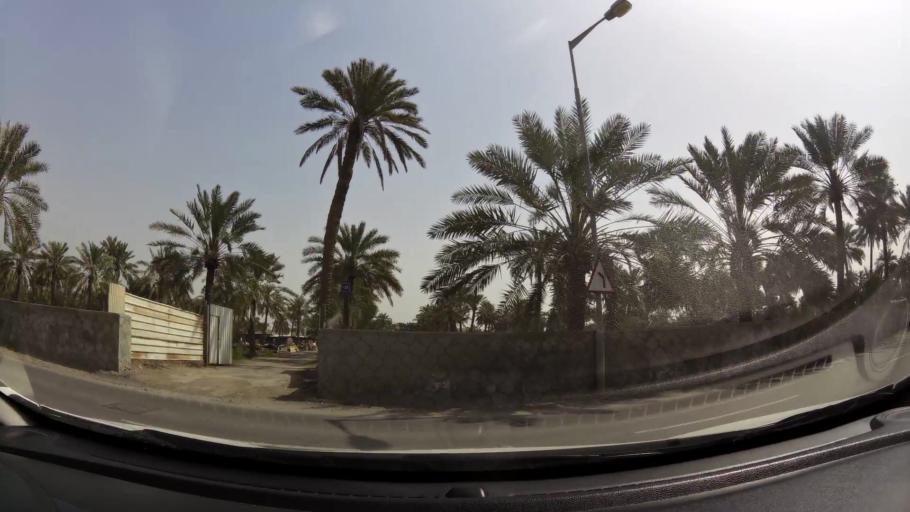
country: BH
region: Manama
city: Jidd Hafs
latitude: 26.2256
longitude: 50.5039
